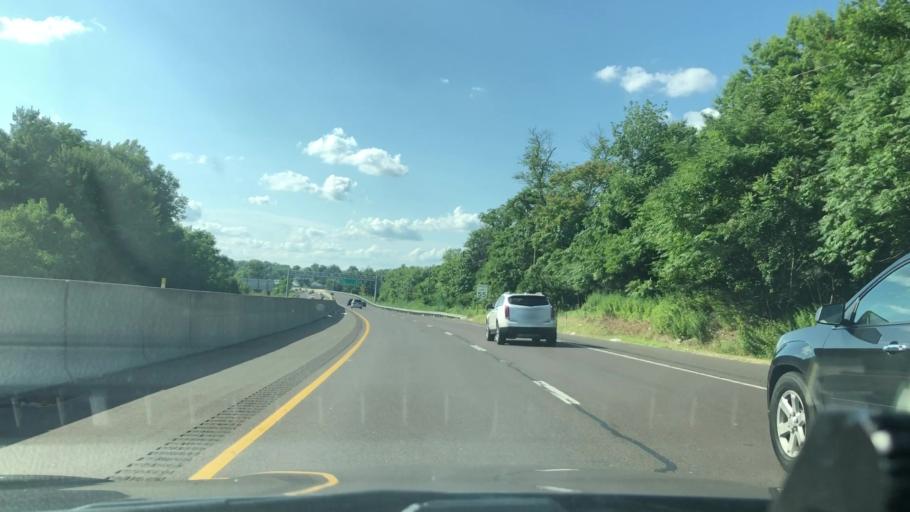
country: US
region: Pennsylvania
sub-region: Montgomery County
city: Spring House
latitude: 40.1866
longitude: -75.2113
